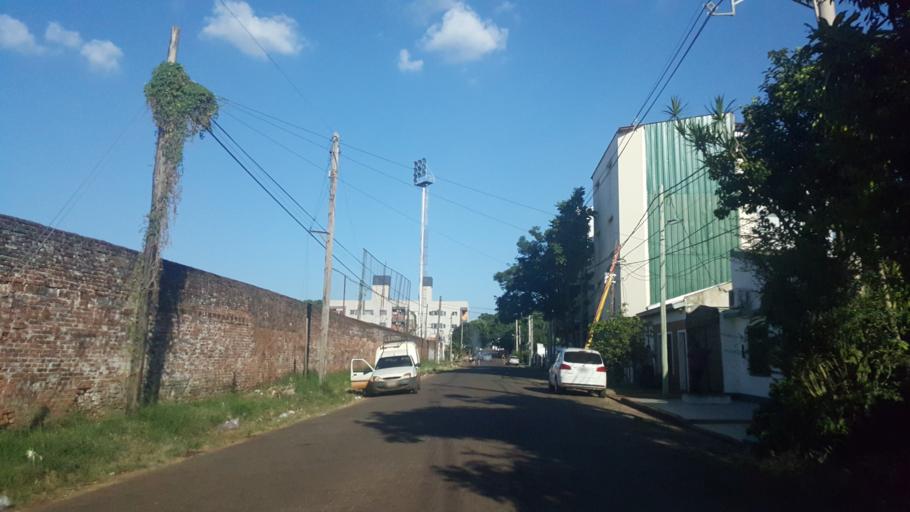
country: AR
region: Misiones
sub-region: Departamento de Capital
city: Posadas
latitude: -27.3862
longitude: -55.8990
